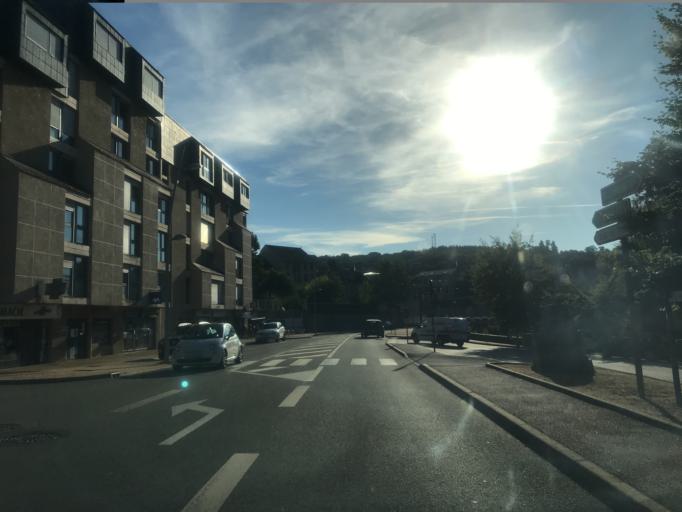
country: FR
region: Limousin
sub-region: Departement de la Creuse
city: Aubusson
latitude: 45.9548
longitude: 2.1707
